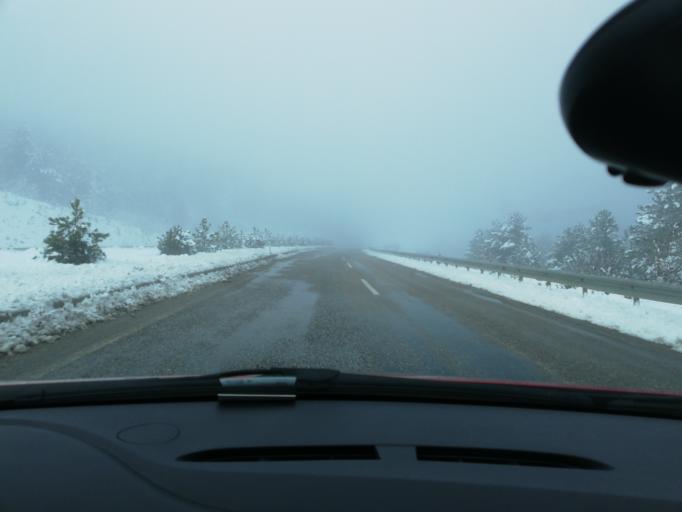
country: TR
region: Kastamonu
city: Akkaya
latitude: 41.2975
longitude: 33.5118
